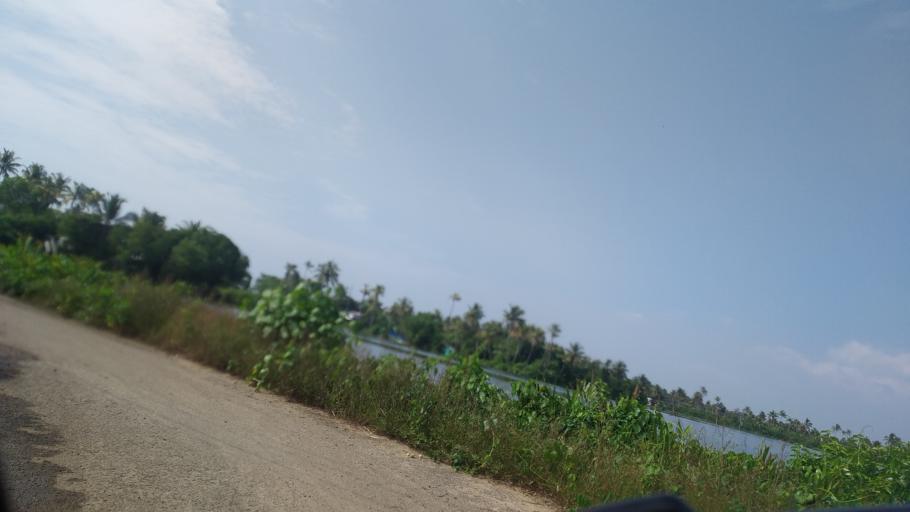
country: IN
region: Kerala
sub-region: Ernakulam
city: Elur
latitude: 10.0810
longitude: 76.1970
